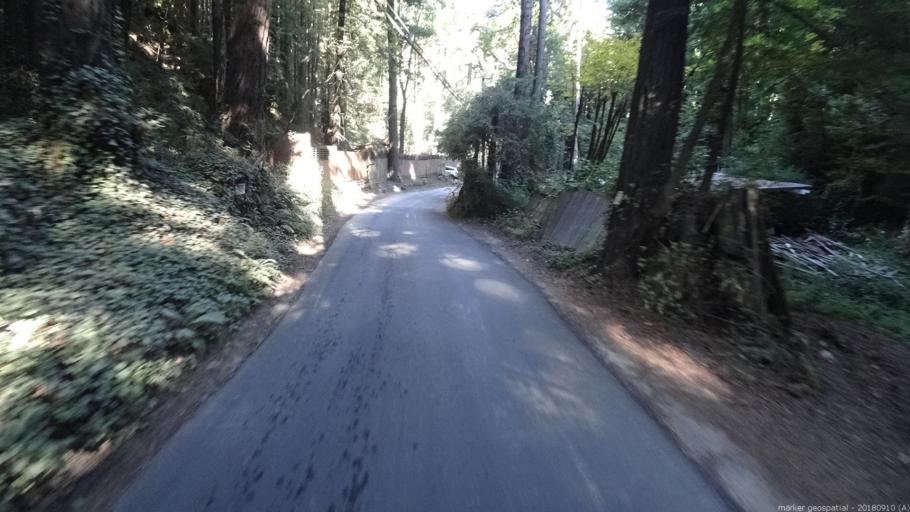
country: US
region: California
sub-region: Monterey County
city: Carmel Valley Village
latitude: 36.3940
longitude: -121.8782
